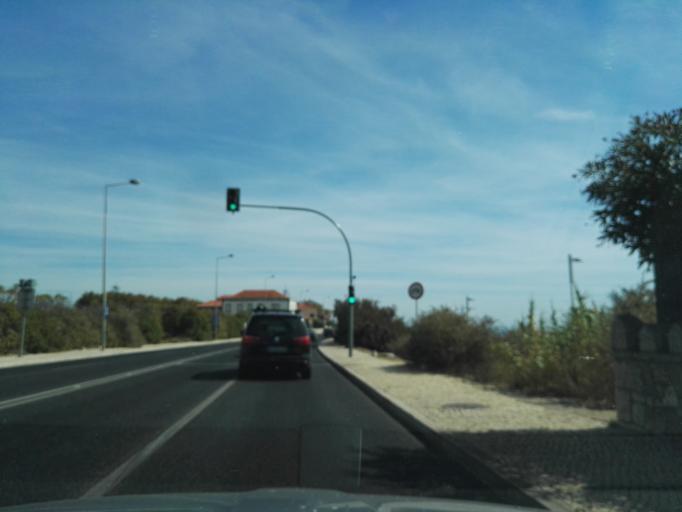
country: PT
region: Lisbon
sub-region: Cascais
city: Estoril
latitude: 38.6964
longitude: -9.3787
